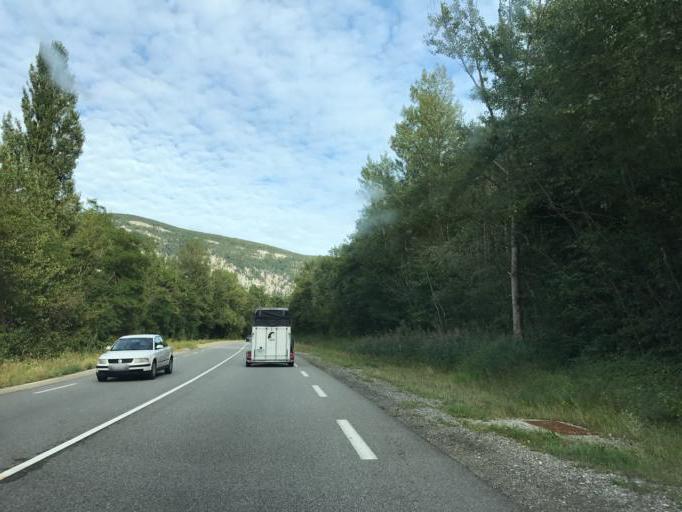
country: FR
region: Rhone-Alpes
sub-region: Departement de l'Ain
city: Collonges
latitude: 46.1022
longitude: 5.8759
